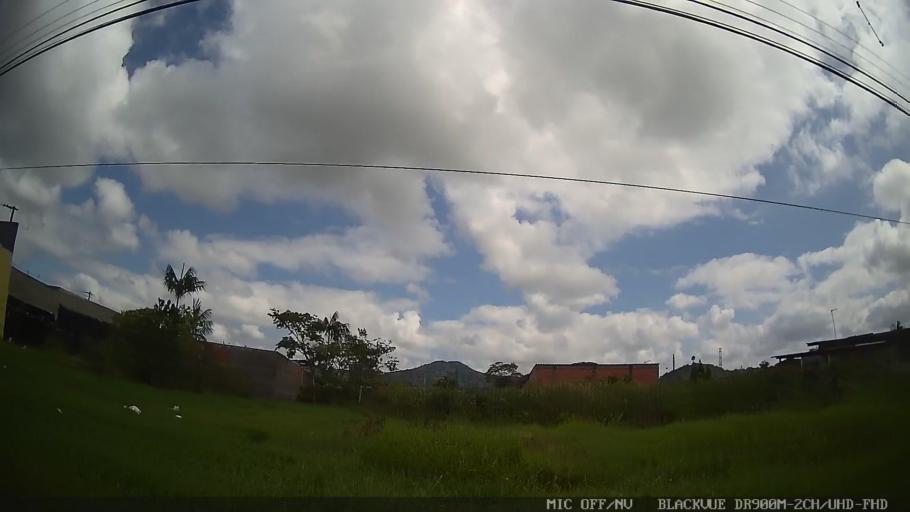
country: BR
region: Sao Paulo
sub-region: Peruibe
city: Peruibe
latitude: -24.2938
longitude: -47.0204
